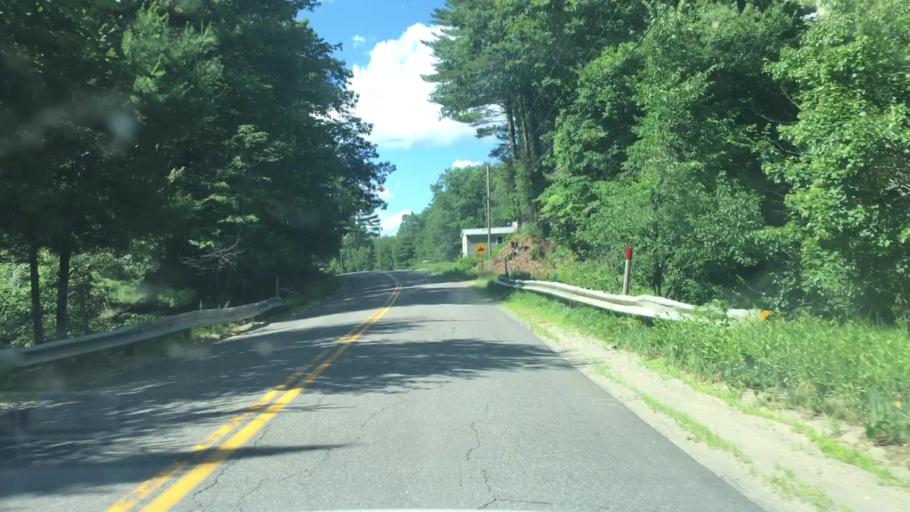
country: US
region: Maine
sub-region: Franklin County
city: Chesterville
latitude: 44.5680
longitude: -70.0870
